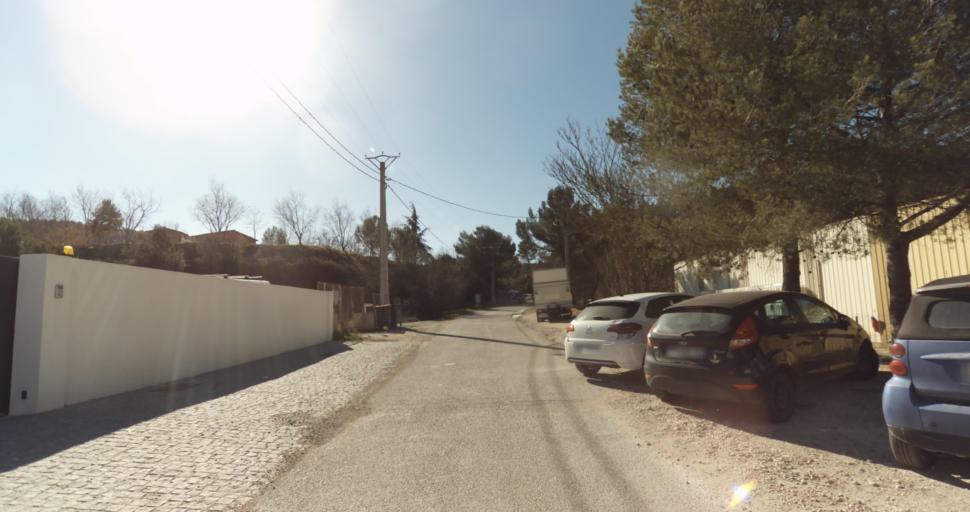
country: FR
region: Provence-Alpes-Cote d'Azur
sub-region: Departement des Bouches-du-Rhone
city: Cadolive
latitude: 43.3959
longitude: 5.5626
